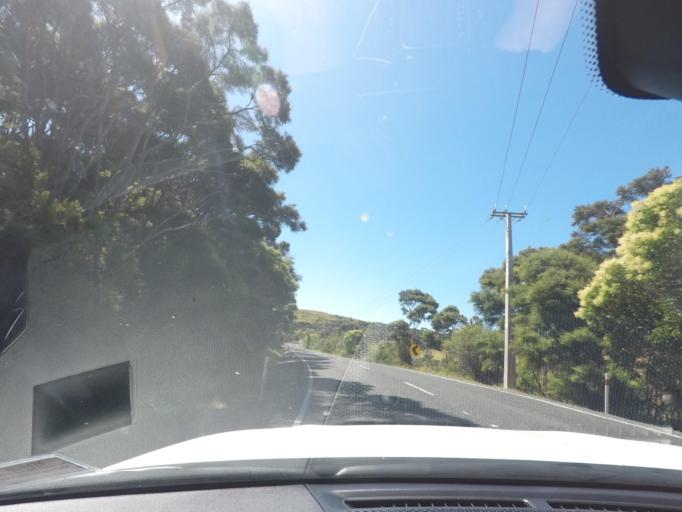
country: NZ
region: Auckland
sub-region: Auckland
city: Parakai
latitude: -36.5990
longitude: 174.3377
